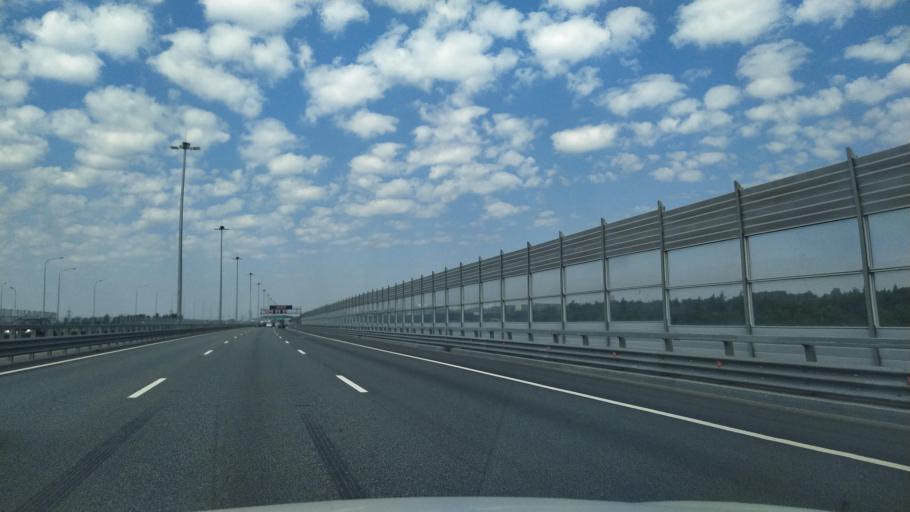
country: RU
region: St.-Petersburg
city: Pargolovo
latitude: 60.0961
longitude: 30.3112
